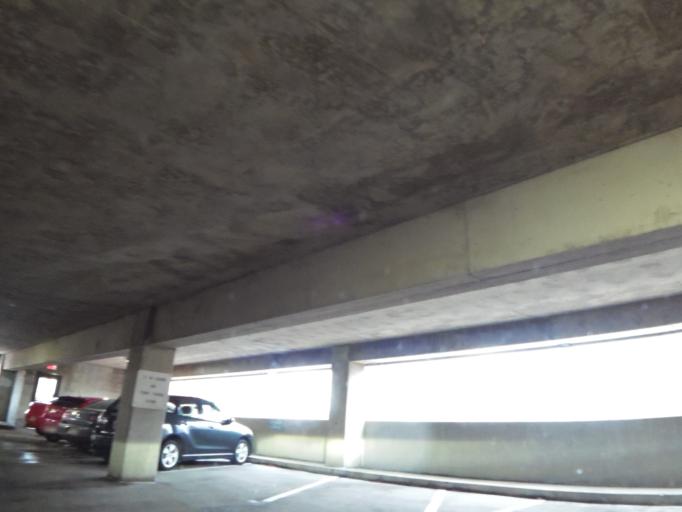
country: US
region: Minnesota
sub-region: Hennepin County
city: Minnetonka Mills
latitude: 44.9262
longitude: -93.4154
